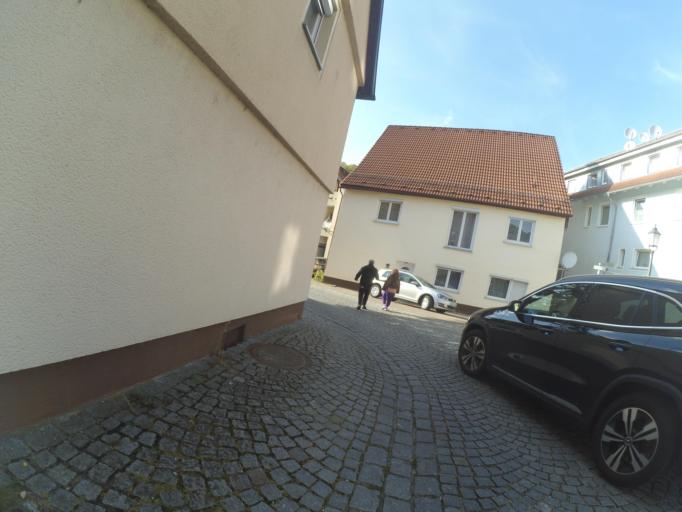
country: DE
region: Baden-Wuerttemberg
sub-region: Regierungsbezirk Stuttgart
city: Heubach
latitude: 48.7890
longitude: 9.9337
